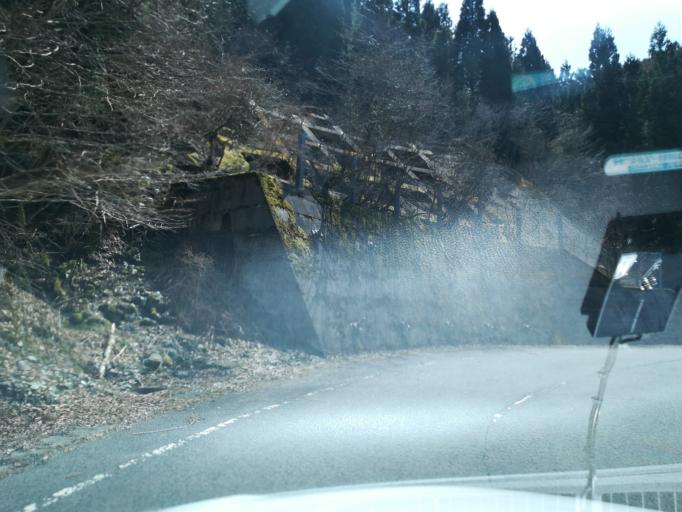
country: JP
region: Tokushima
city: Wakimachi
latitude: 33.8803
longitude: 134.0554
